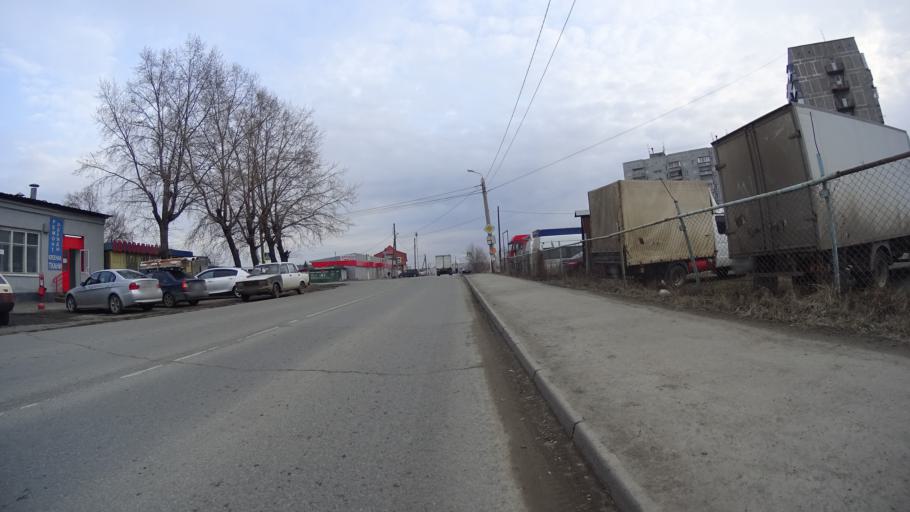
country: RU
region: Chelyabinsk
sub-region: Gorod Chelyabinsk
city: Chelyabinsk
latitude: 55.1902
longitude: 61.4763
